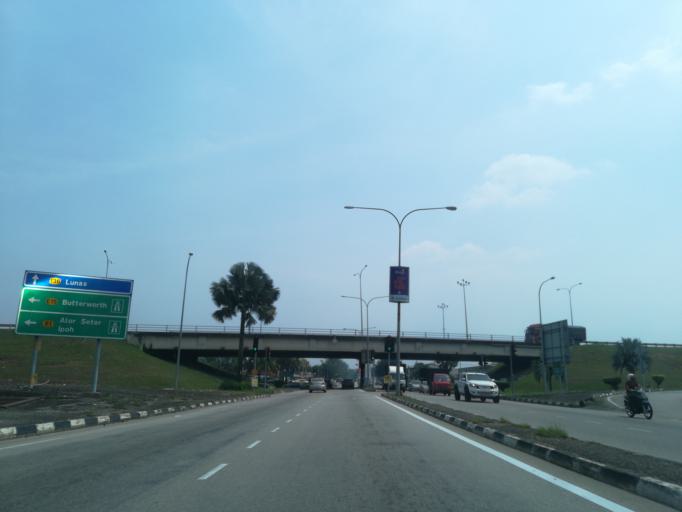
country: MY
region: Kedah
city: Kulim
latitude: 5.4196
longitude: 100.5378
